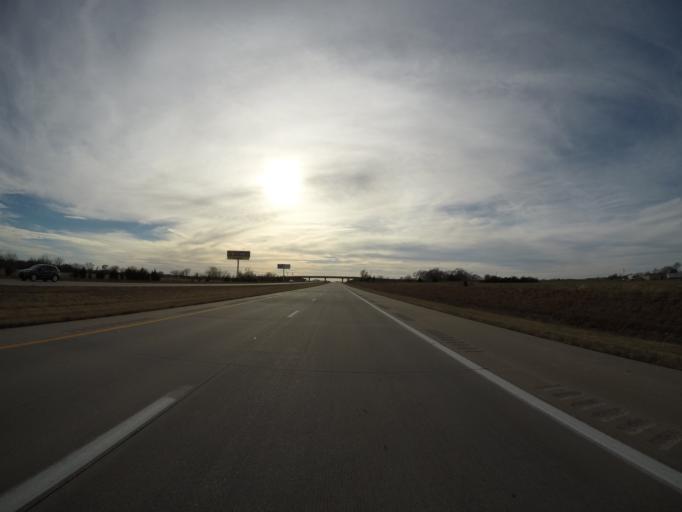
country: US
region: Kansas
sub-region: Franklin County
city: Wellsville
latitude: 38.6870
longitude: -95.1180
